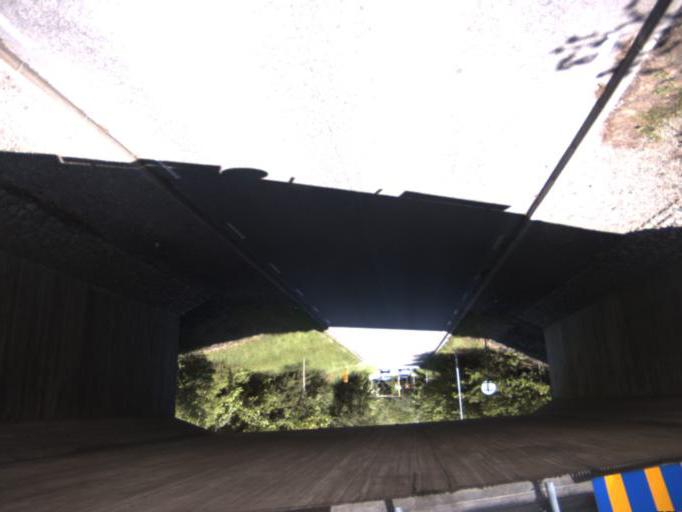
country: SE
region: Skane
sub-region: Helsingborg
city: Rydeback
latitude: 55.9981
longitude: 12.7621
